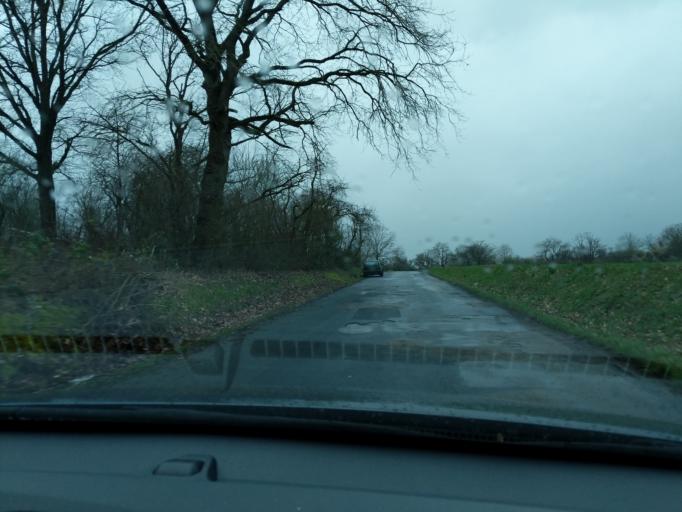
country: DE
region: Hesse
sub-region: Regierungsbezirk Darmstadt
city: Bad Vilbel
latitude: 50.1488
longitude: 8.7156
